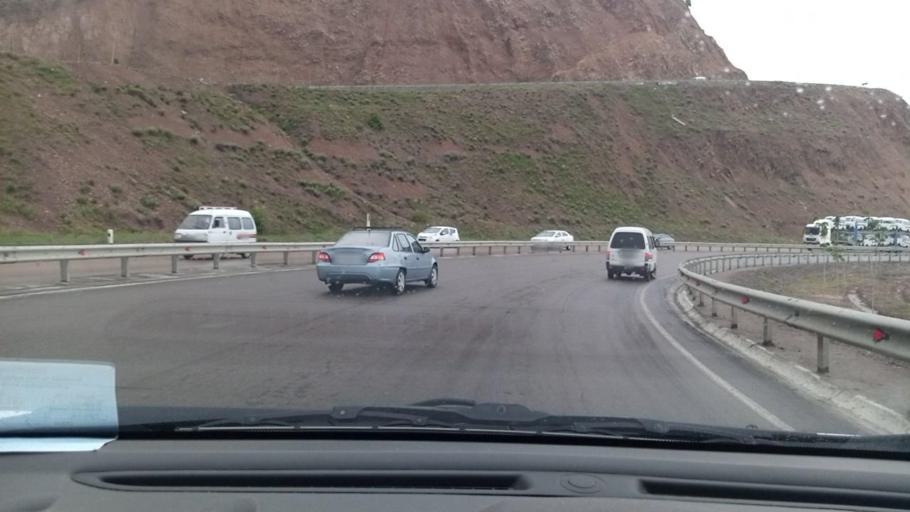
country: UZ
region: Toshkent
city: Angren
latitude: 41.1131
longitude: 70.5044
